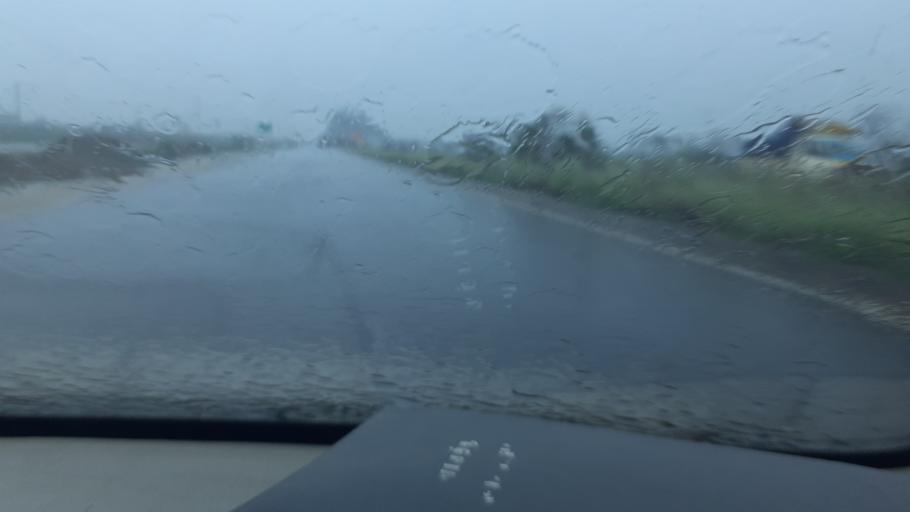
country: IN
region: Tamil Nadu
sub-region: Virudhunagar
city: Sattur
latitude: 9.4412
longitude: 77.9249
